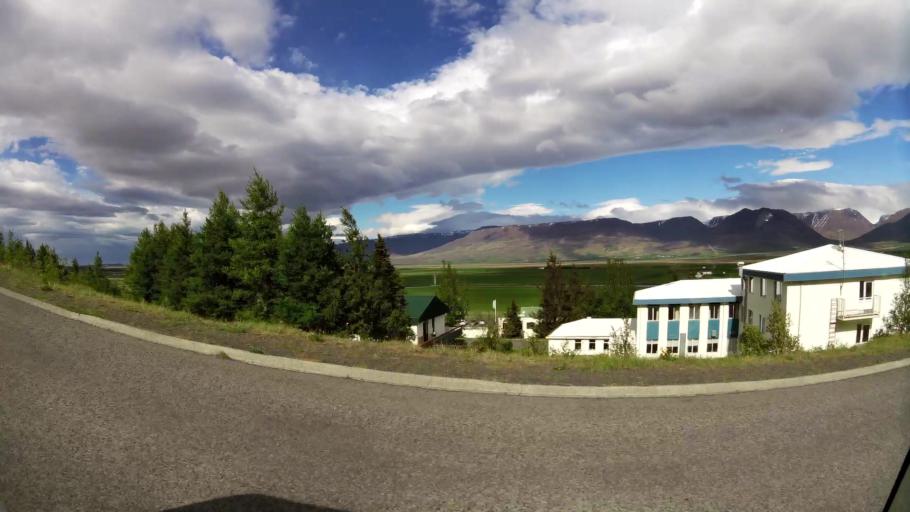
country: IS
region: Northwest
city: Saudarkrokur
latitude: 65.5529
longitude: -19.4485
